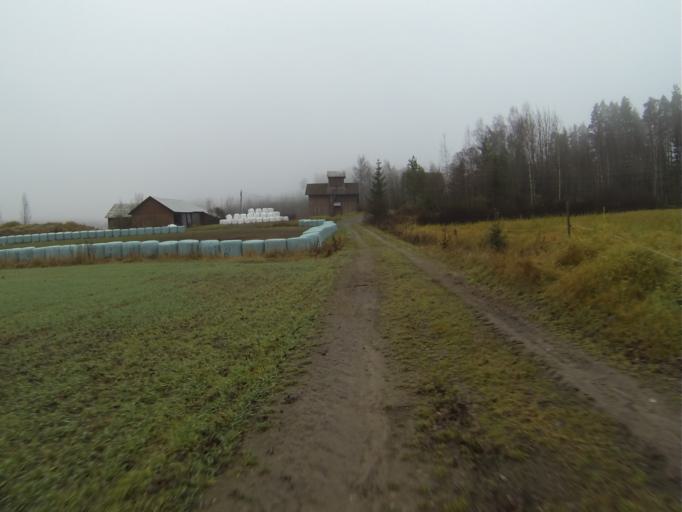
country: FI
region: Varsinais-Suomi
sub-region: Salo
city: Halikko
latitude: 60.4074
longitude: 22.9587
